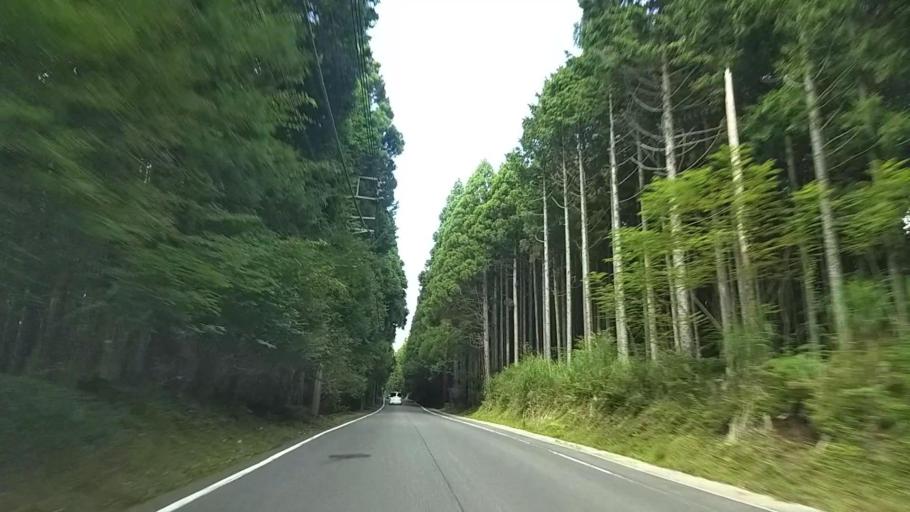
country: JP
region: Shizuoka
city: Gotemba
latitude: 35.2555
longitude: 138.8296
